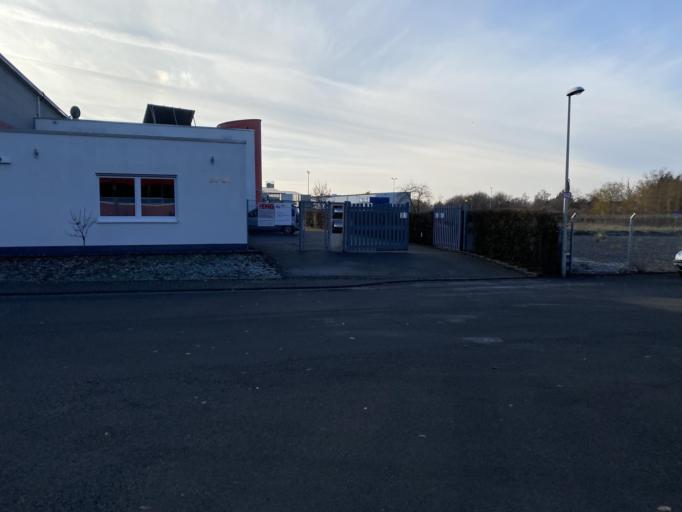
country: DE
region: North Rhine-Westphalia
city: Sankt Augustin
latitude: 50.7539
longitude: 7.1633
